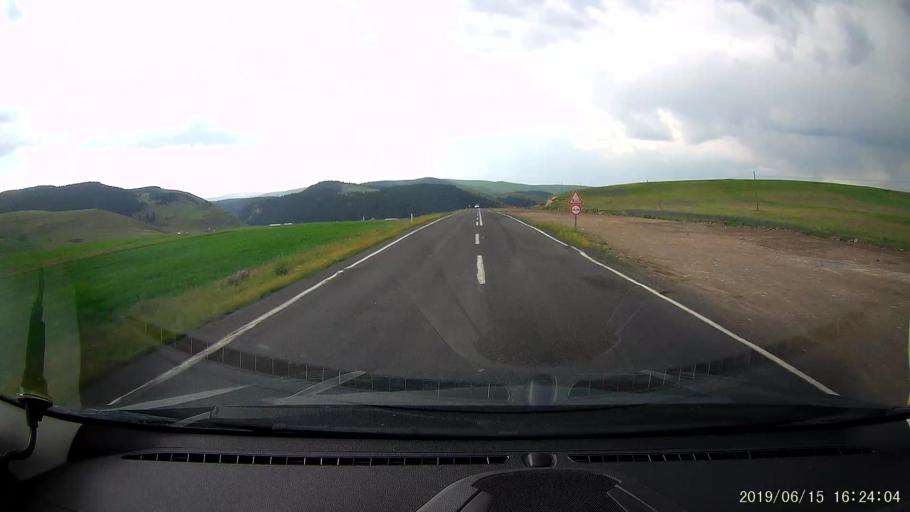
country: TR
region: Ardahan
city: Hanak
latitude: 41.1698
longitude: 42.8681
